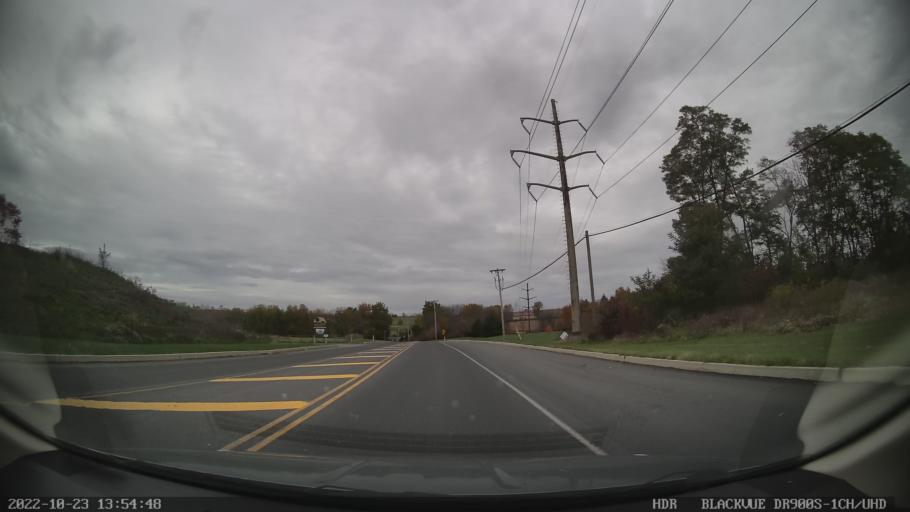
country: US
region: Pennsylvania
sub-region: Northampton County
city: North Catasauqua
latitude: 40.6748
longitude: -75.4602
